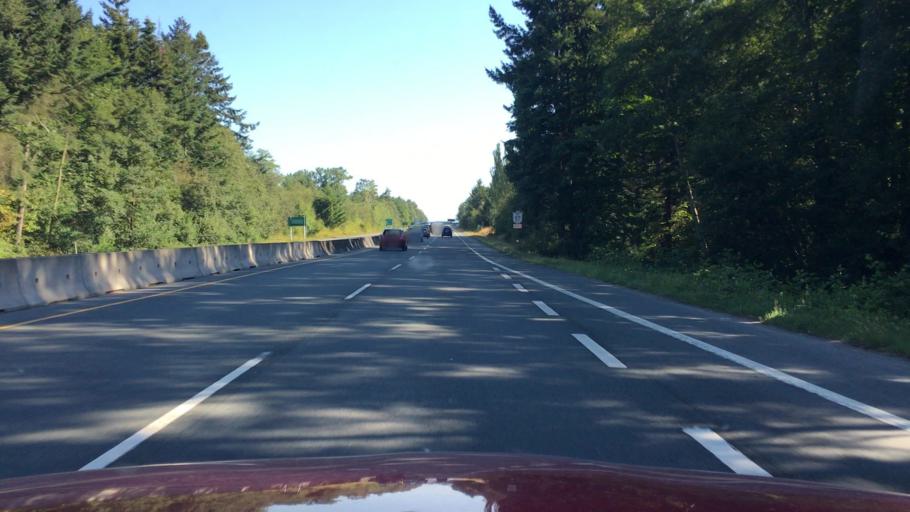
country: CA
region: British Columbia
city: North Saanich
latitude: 48.6343
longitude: -123.4102
